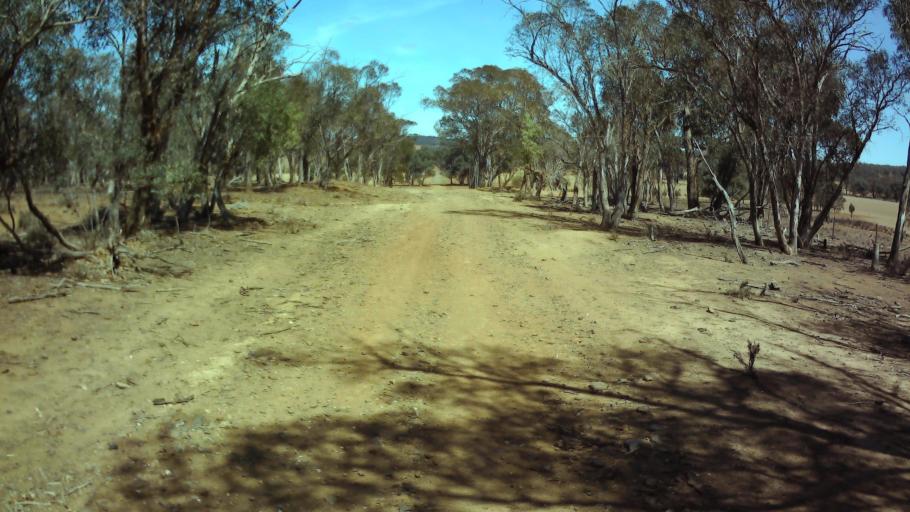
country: AU
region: New South Wales
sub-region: Forbes
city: Forbes
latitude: -33.7167
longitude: 147.8105
